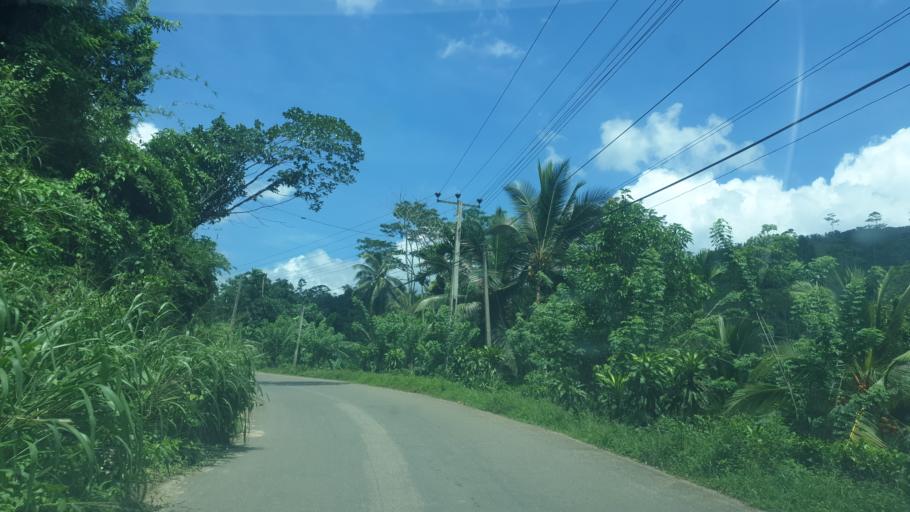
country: LK
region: Sabaragamuwa
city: Ratnapura
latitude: 6.4851
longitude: 80.4054
